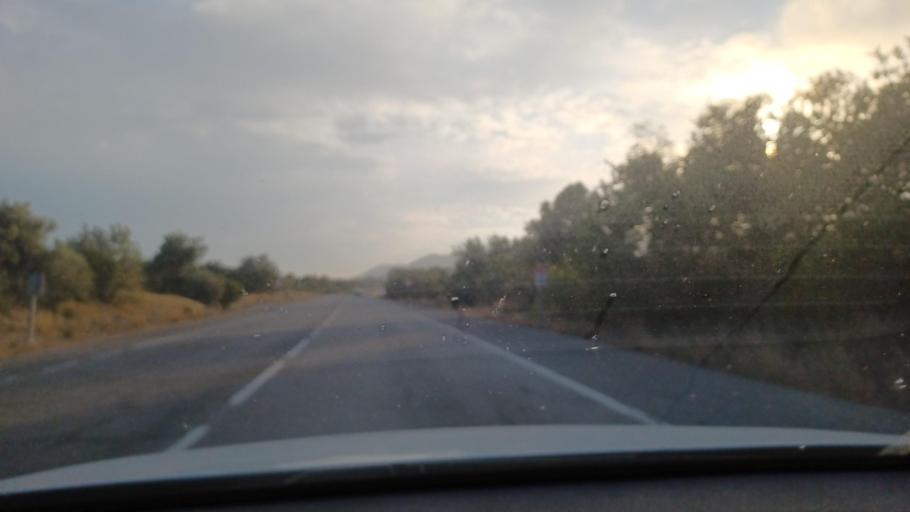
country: ES
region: Catalonia
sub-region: Provincia de Tarragona
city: Colldejou
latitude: 40.9924
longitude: 0.9130
